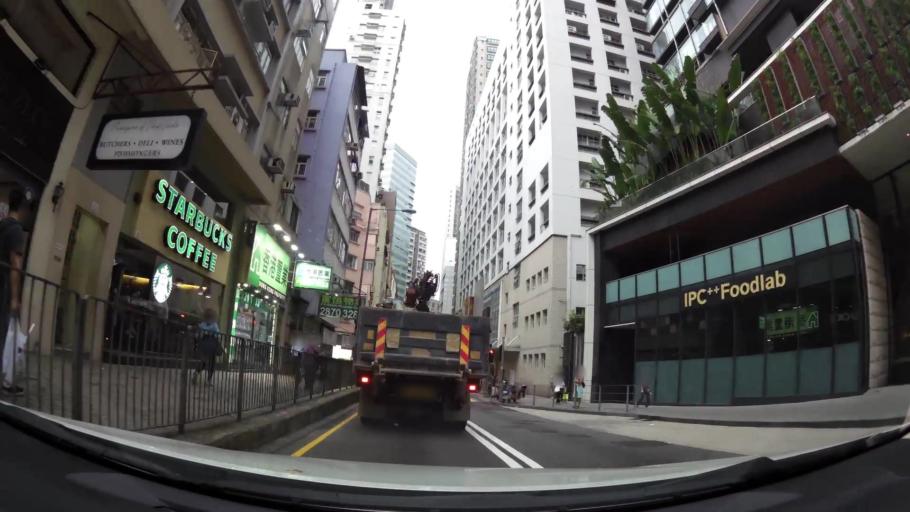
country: HK
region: Central and Western
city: Central
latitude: 22.2808
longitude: 114.1524
